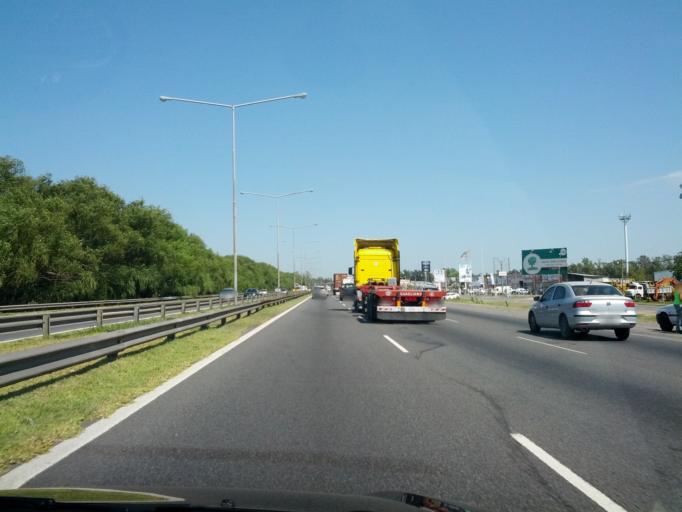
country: AR
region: Buenos Aires
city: Belen de Escobar
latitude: -34.3713
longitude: -58.7673
